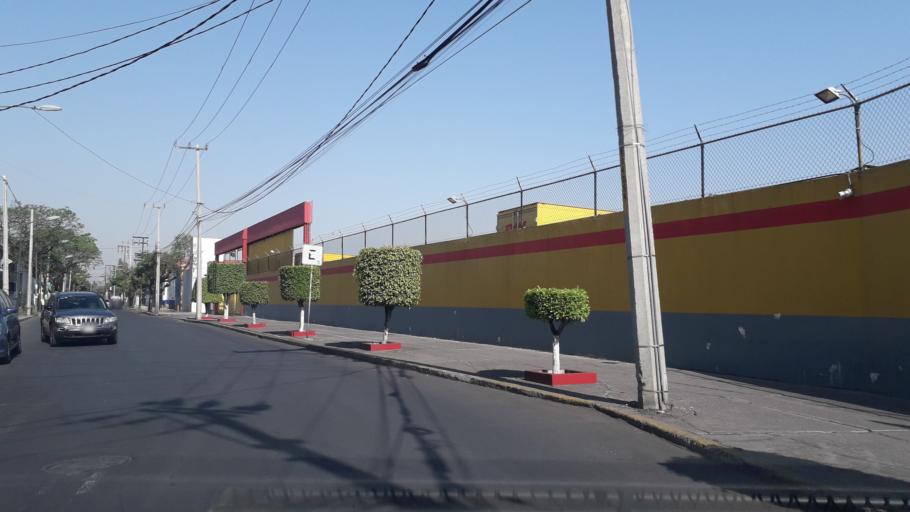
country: MX
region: Mexico City
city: Venustiano Carranza
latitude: 19.4236
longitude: -99.0908
